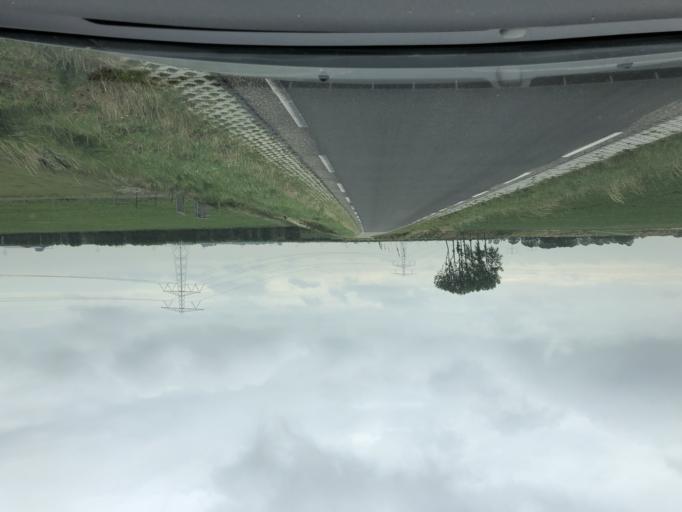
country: NL
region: Zeeland
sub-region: Gemeente Reimerswaal
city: Yerseke
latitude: 51.4640
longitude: 4.0512
